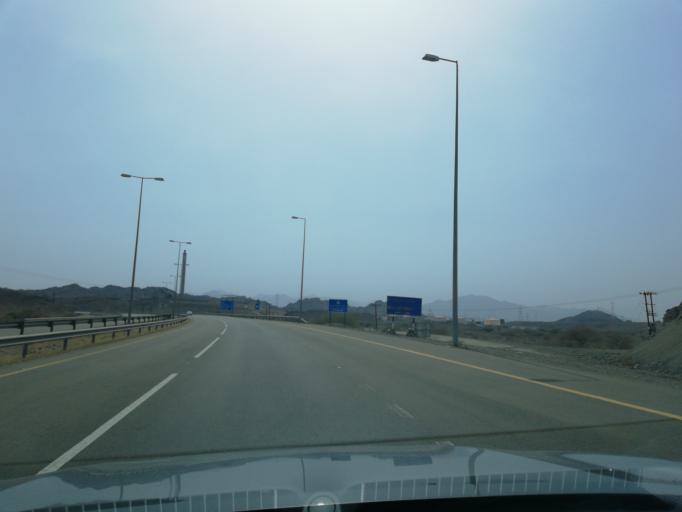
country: OM
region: Al Batinah
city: Al Liwa'
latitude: 24.3065
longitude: 56.4321
